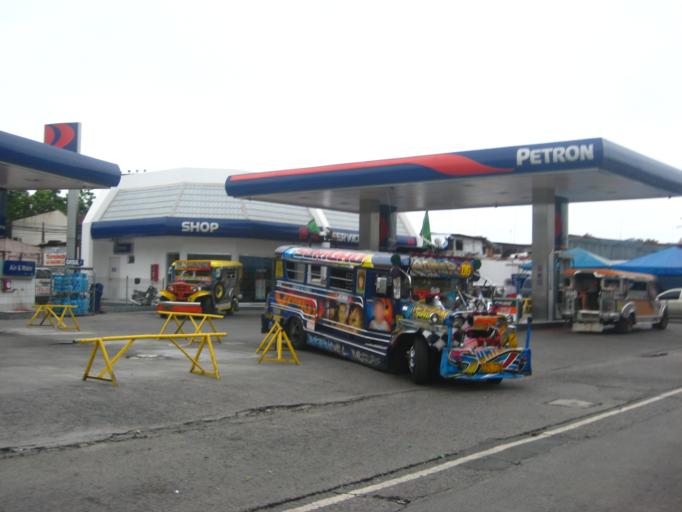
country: PH
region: Calabarzon
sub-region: Province of Rizal
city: Pateros
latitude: 14.5398
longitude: 121.0674
